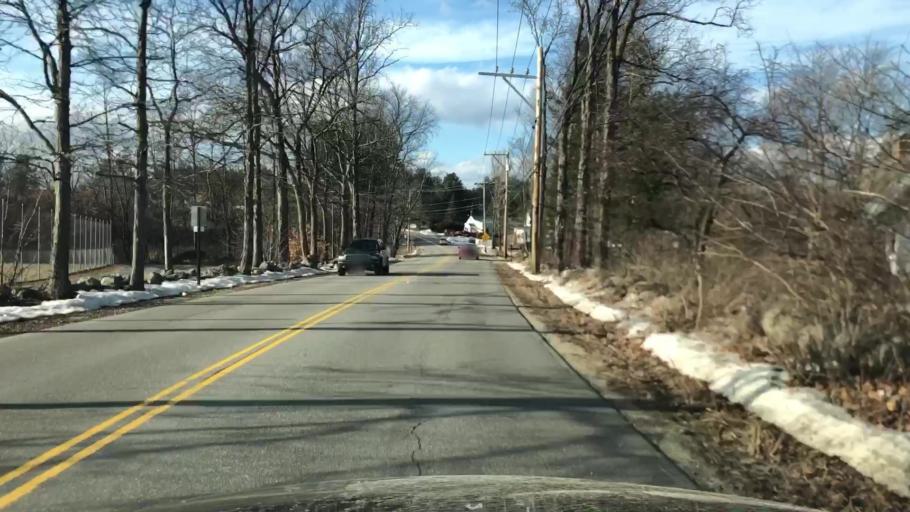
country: US
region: New Hampshire
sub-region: Hillsborough County
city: Milford
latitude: 42.8419
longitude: -71.6610
